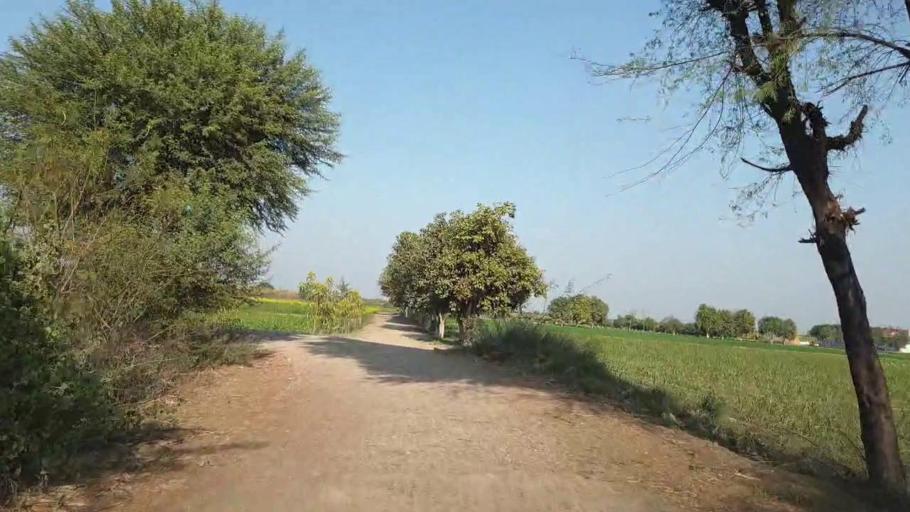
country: PK
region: Sindh
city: Tando Jam
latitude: 25.5066
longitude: 68.5383
